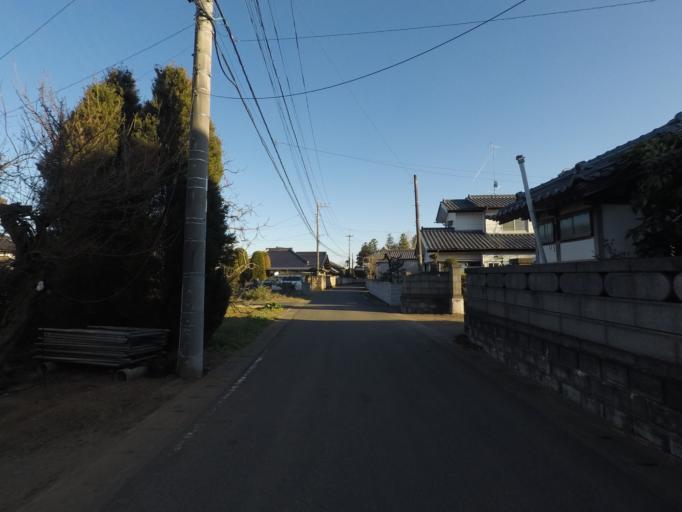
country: JP
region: Ibaraki
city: Ishige
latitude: 36.1073
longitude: 140.0294
